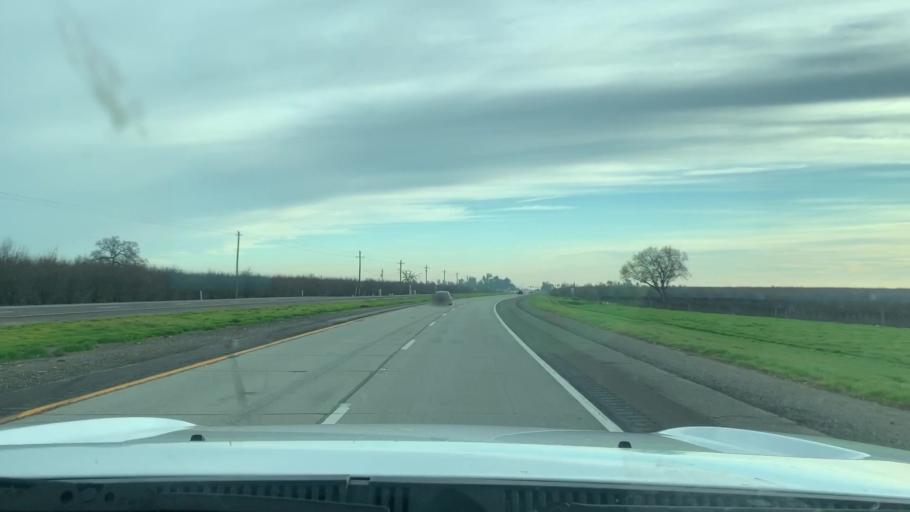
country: US
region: California
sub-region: Kings County
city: Lemoore
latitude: 36.3528
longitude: -119.8084
